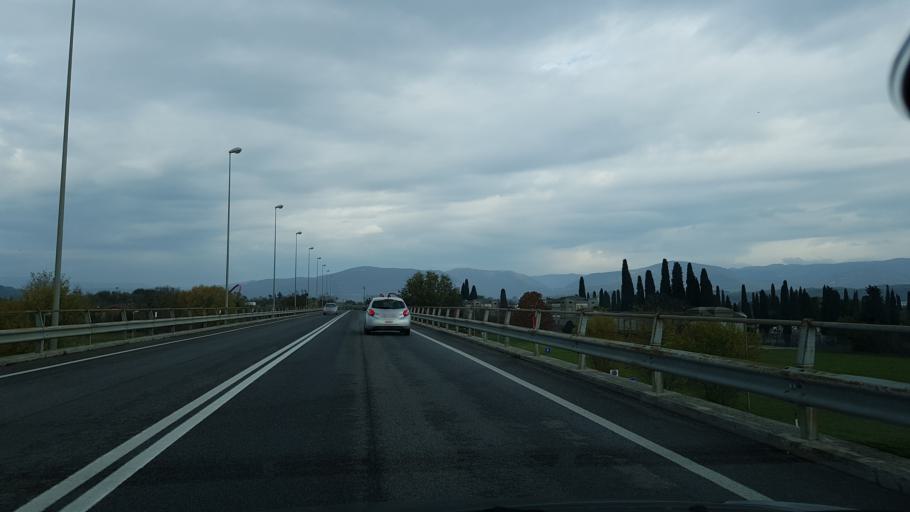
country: SI
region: Miren-Kostanjevica
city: Miren
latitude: 45.9127
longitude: 13.6124
